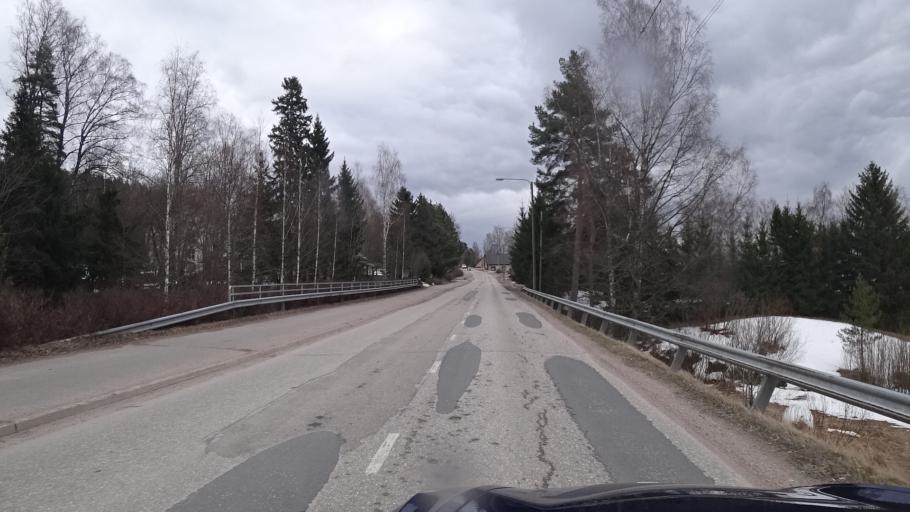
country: FI
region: Paijanne Tavastia
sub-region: Lahti
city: Nastola
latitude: 60.8759
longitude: 26.0006
